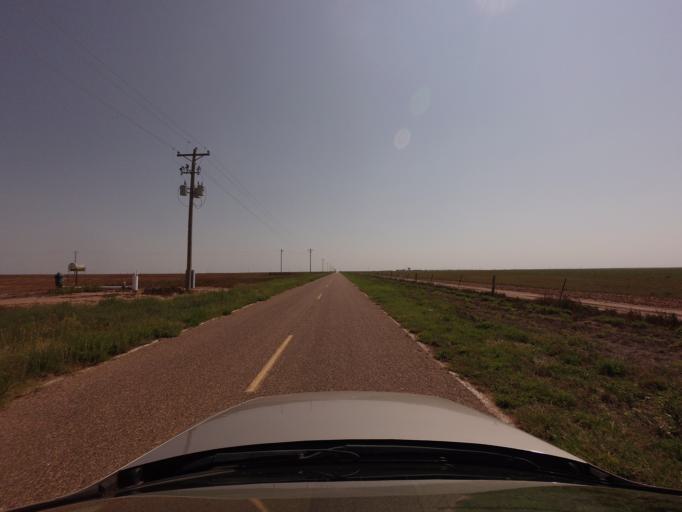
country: US
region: New Mexico
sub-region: Curry County
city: Cannon Air Force Base
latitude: 34.6329
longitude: -103.3475
